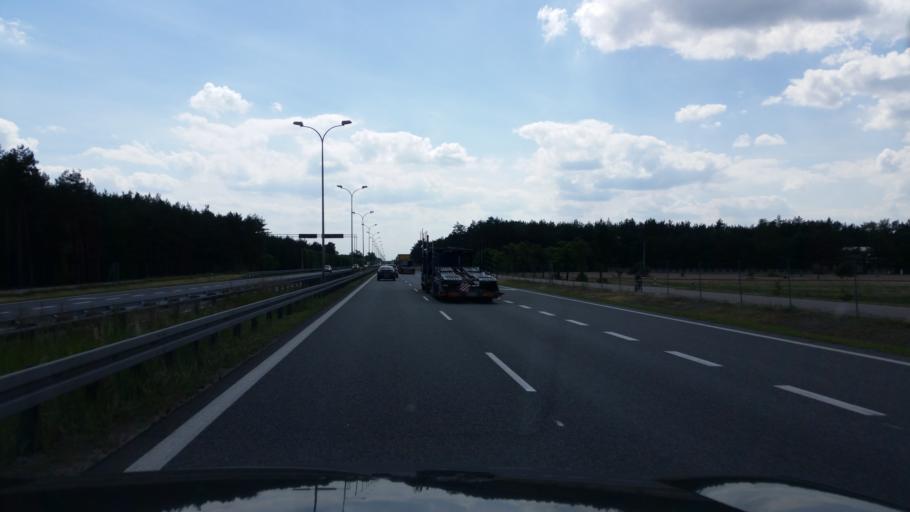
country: PL
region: Masovian Voivodeship
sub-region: Powiat wyszkowski
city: Wyszkow
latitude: 52.5312
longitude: 21.4248
